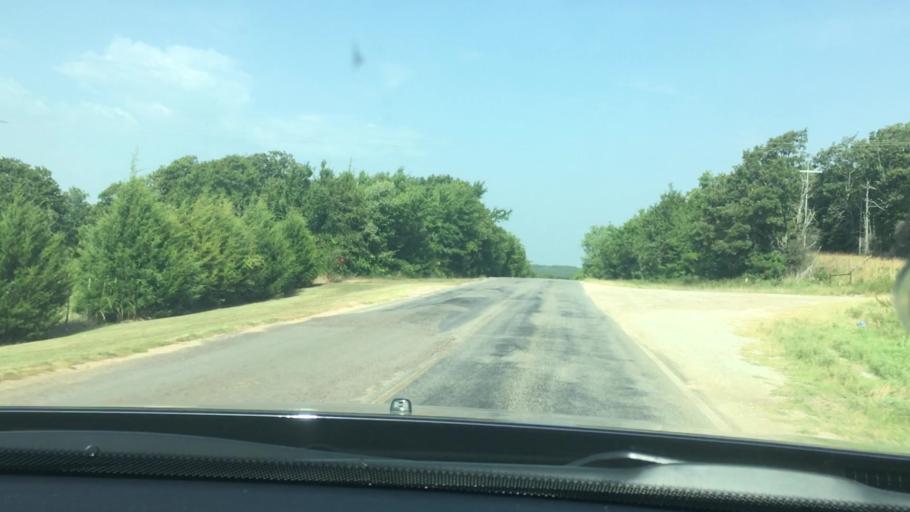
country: US
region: Oklahoma
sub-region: Pontotoc County
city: Byng
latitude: 34.8648
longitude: -96.6149
